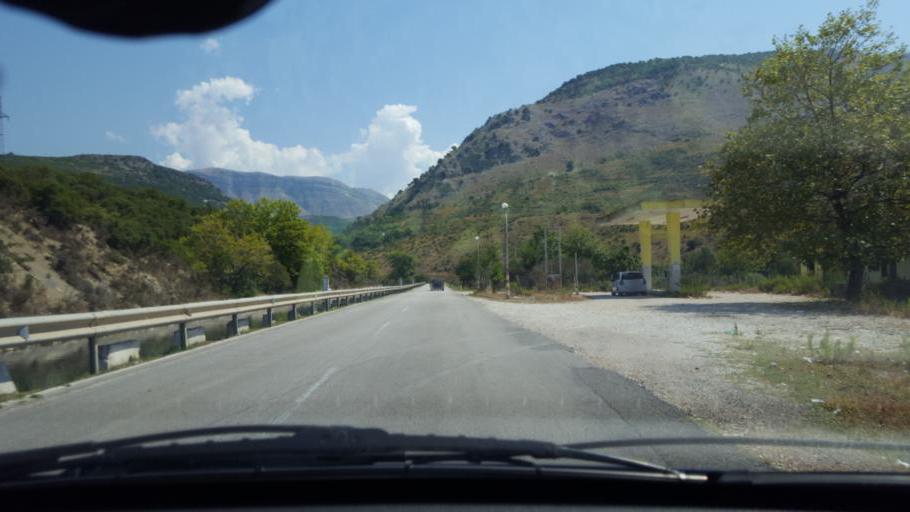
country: AL
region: Vlore
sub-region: Rrethi i Delvines
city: Mesopotam
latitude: 39.9119
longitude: 20.1285
